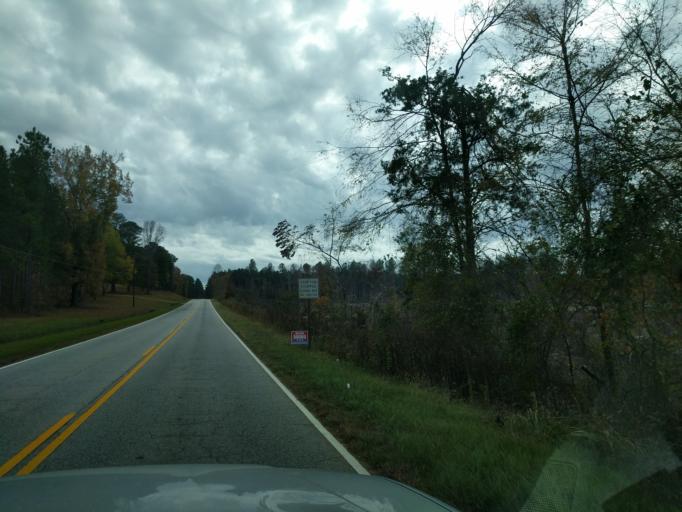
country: US
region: South Carolina
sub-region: Greenwood County
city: Ninety Six
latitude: 34.1721
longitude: -81.8622
